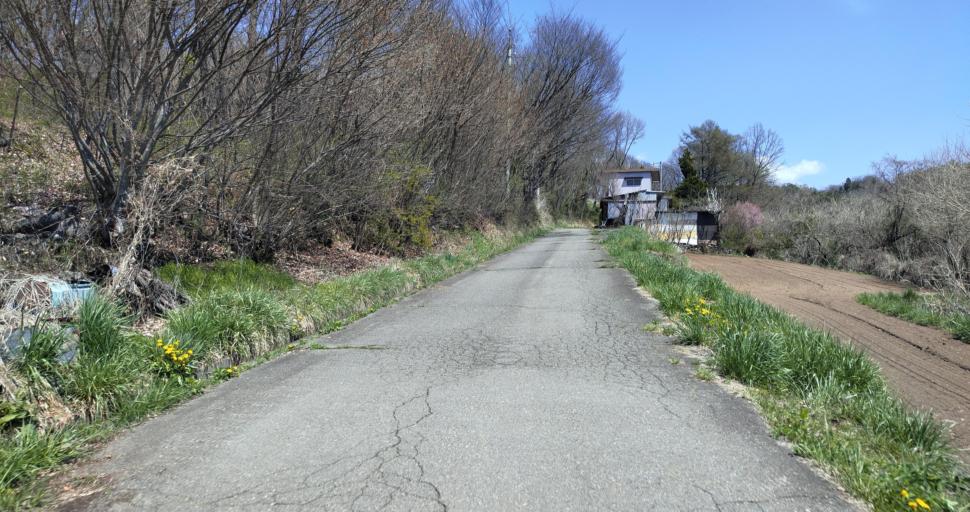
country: JP
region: Nagano
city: Komoro
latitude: 36.3599
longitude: 138.3923
